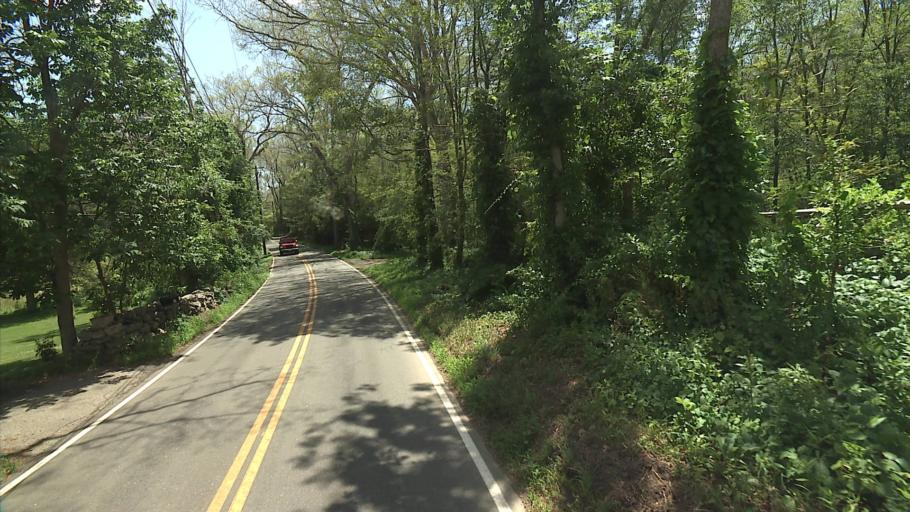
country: US
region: Connecticut
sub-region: Middlesex County
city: Essex Village
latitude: 41.4496
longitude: -72.3389
